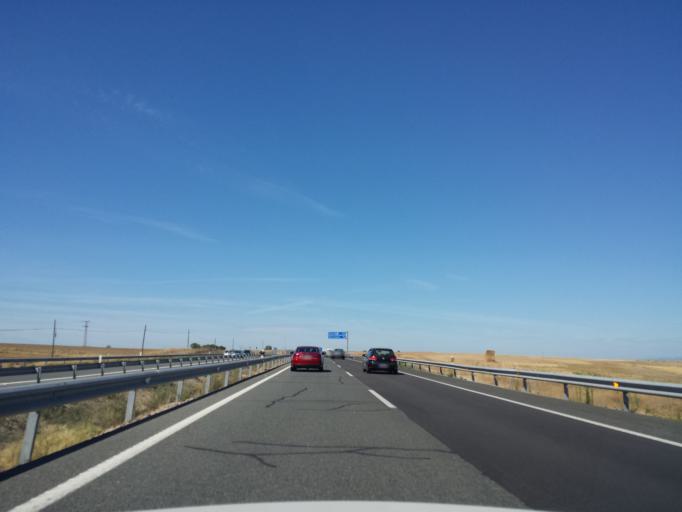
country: ES
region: Castille-La Mancha
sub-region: Province of Toledo
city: Herreruela de Oropesa
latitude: 39.9045
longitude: -5.2333
